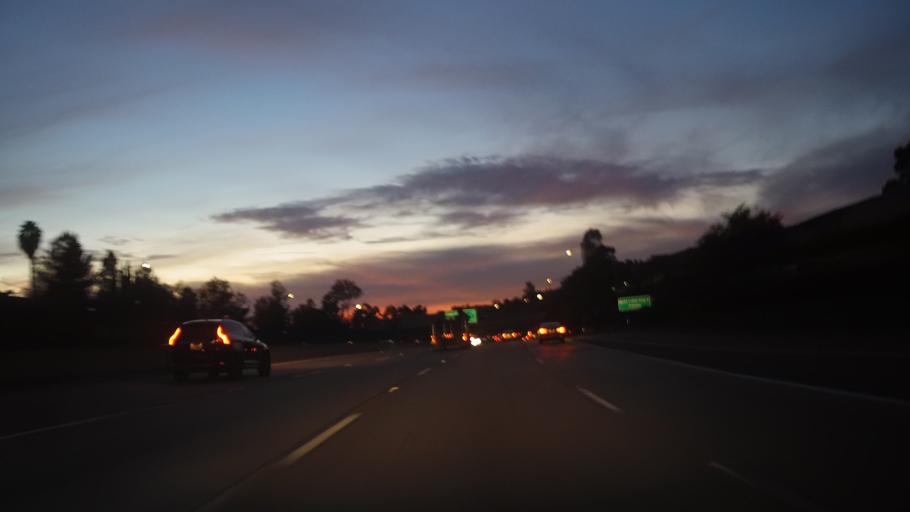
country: US
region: California
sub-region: San Diego County
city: Lemon Grove
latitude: 32.7475
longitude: -117.0224
